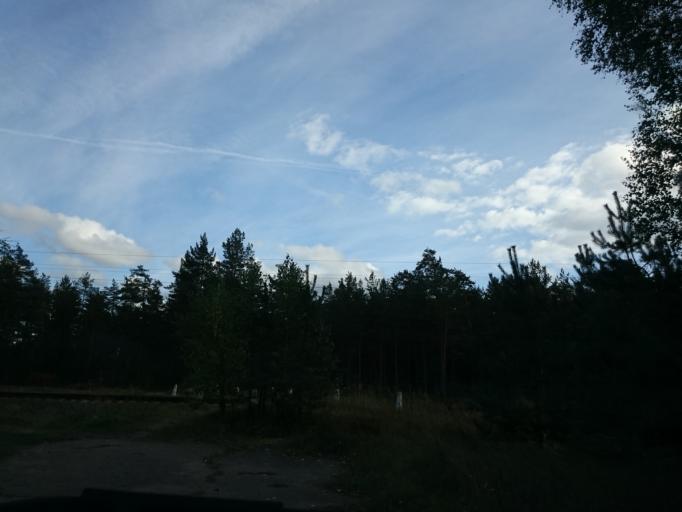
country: LV
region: Garkalne
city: Garkalne
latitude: 57.0392
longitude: 24.3896
